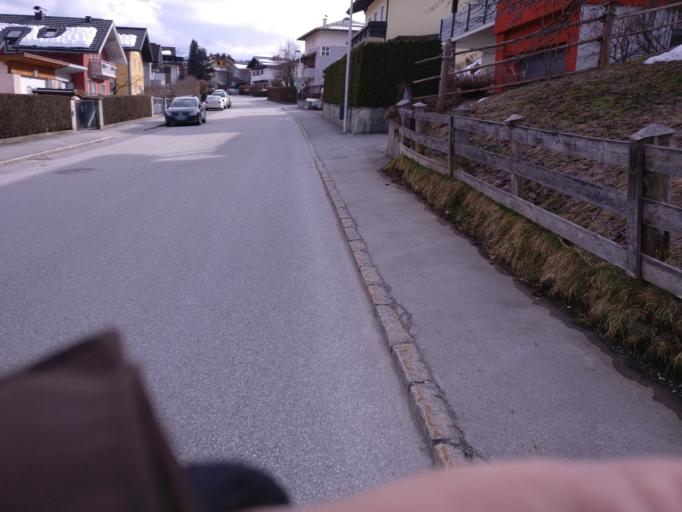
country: AT
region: Salzburg
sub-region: Politischer Bezirk Sankt Johann im Pongau
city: Bischofshofen
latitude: 47.4208
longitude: 13.2145
